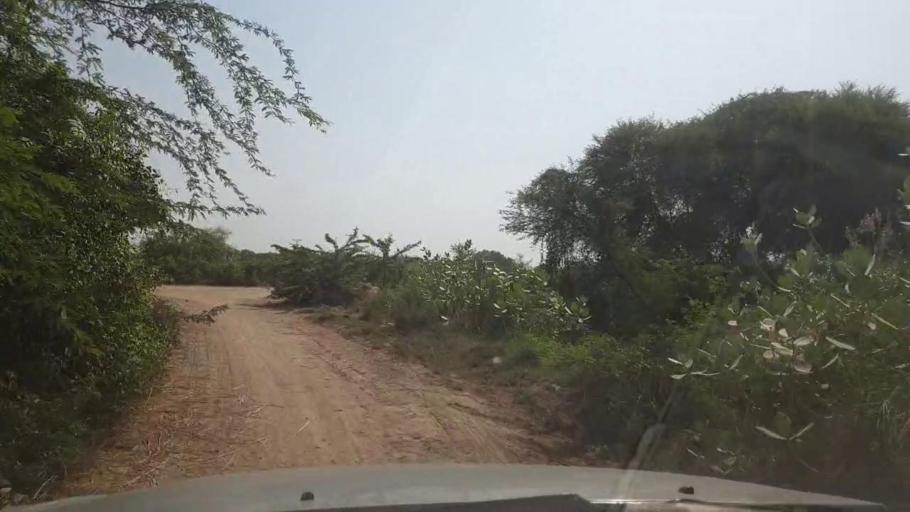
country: PK
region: Sindh
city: Bulri
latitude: 24.8644
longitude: 68.3109
